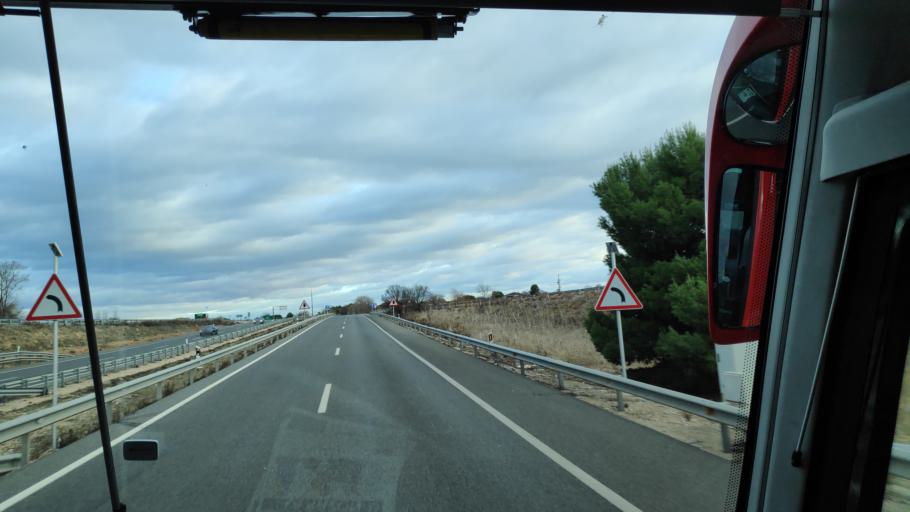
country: ES
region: Madrid
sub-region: Provincia de Madrid
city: Villarejo de Salvanes
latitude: 40.1716
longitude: -3.2922
